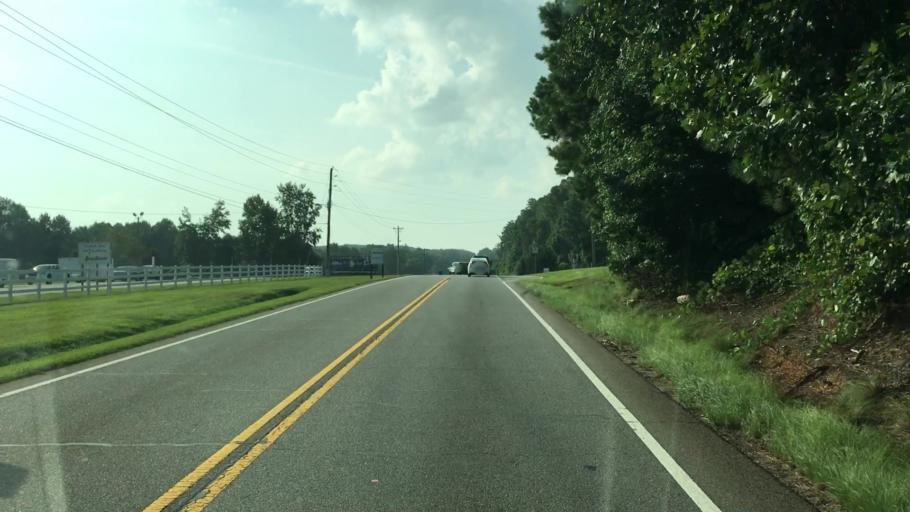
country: US
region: Georgia
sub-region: Jackson County
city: Braselton
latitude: 34.1534
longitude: -83.8155
